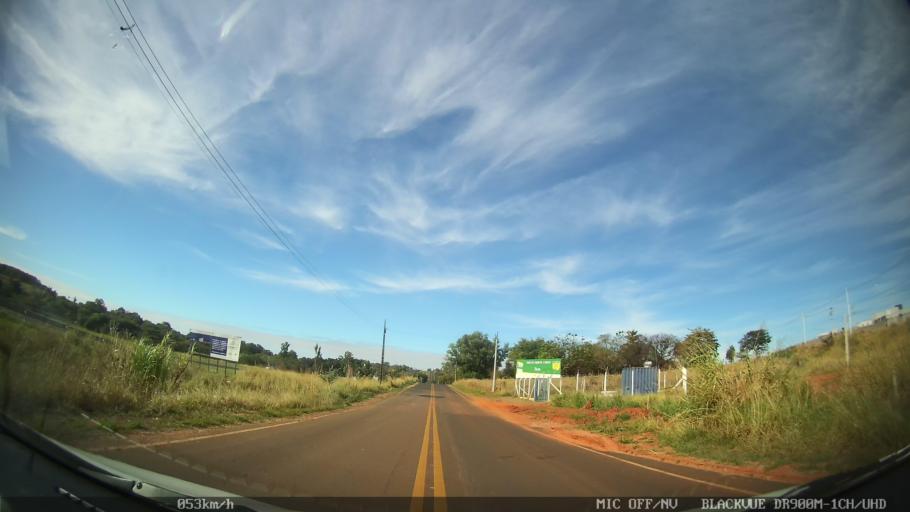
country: BR
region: Sao Paulo
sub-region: Sao Jose Do Rio Preto
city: Sao Jose do Rio Preto
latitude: -20.7970
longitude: -49.3213
